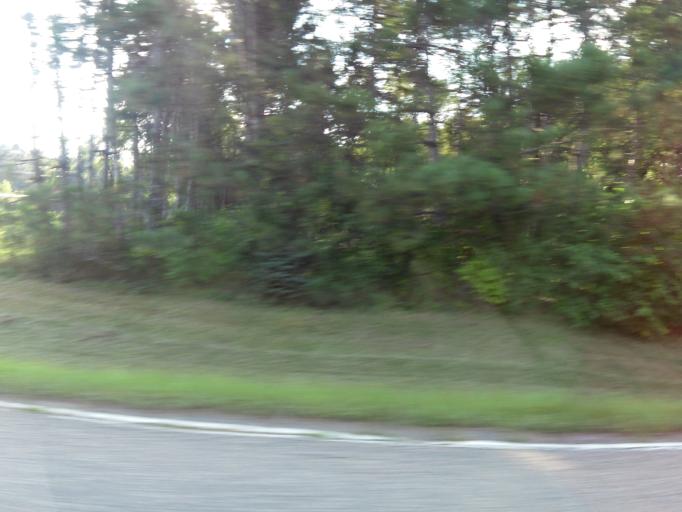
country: US
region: Minnesota
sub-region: Washington County
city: Oak Park Heights
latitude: 44.9866
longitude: -92.8224
